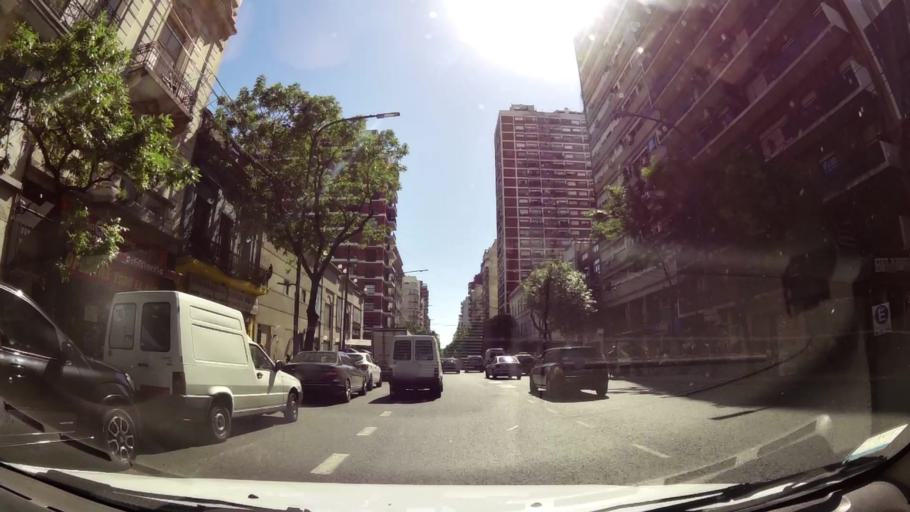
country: AR
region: Buenos Aires F.D.
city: Buenos Aires
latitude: -34.6094
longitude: -58.3956
